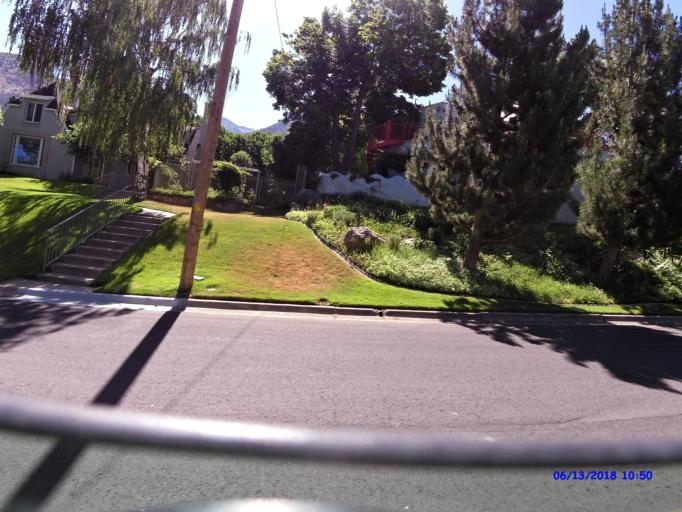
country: US
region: Utah
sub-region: Weber County
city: Ogden
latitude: 41.2154
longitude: -111.9412
